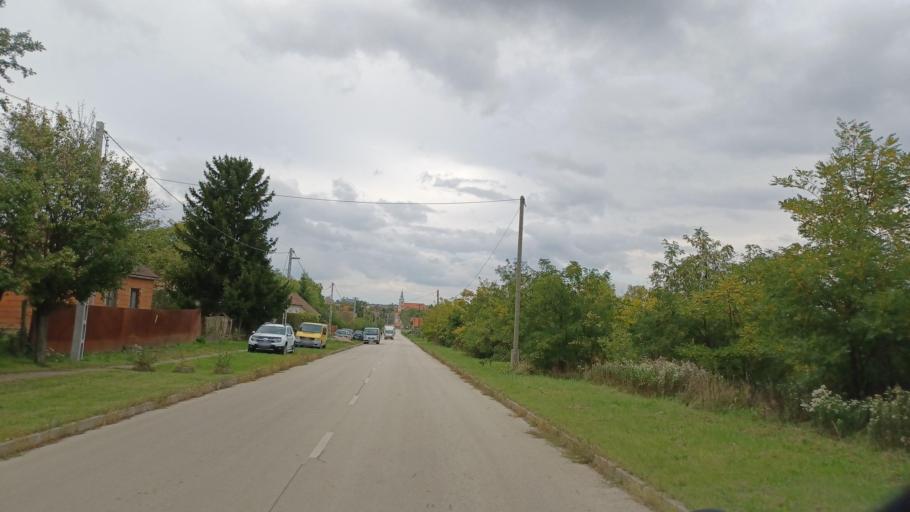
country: HU
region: Tolna
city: Simontornya
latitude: 46.7450
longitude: 18.5592
